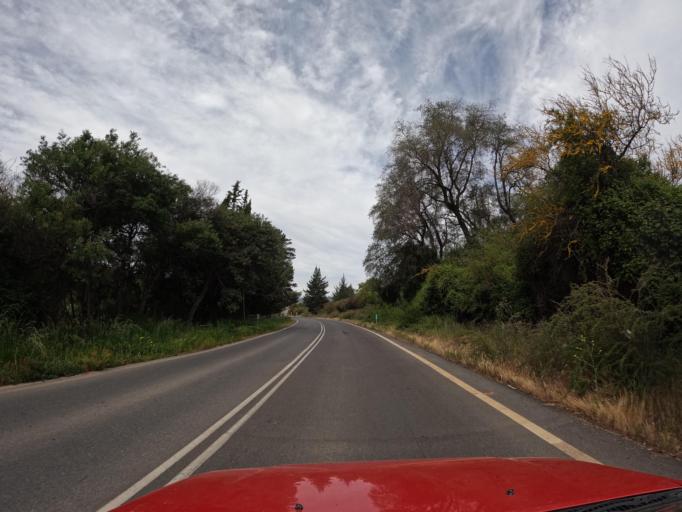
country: CL
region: Maule
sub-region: Provincia de Talca
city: Talca
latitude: -35.3231
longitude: -71.9399
